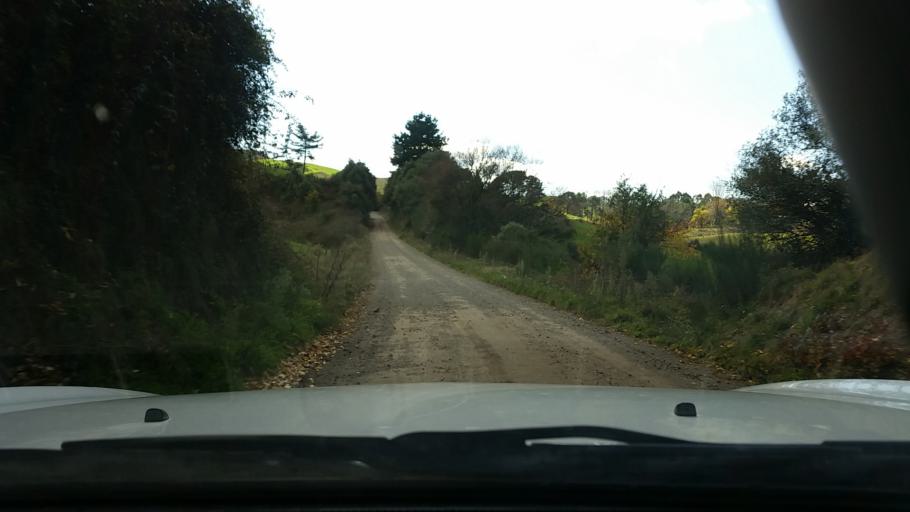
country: NZ
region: Waikato
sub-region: South Waikato District
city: Tokoroa
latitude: -38.3893
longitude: 176.0779
